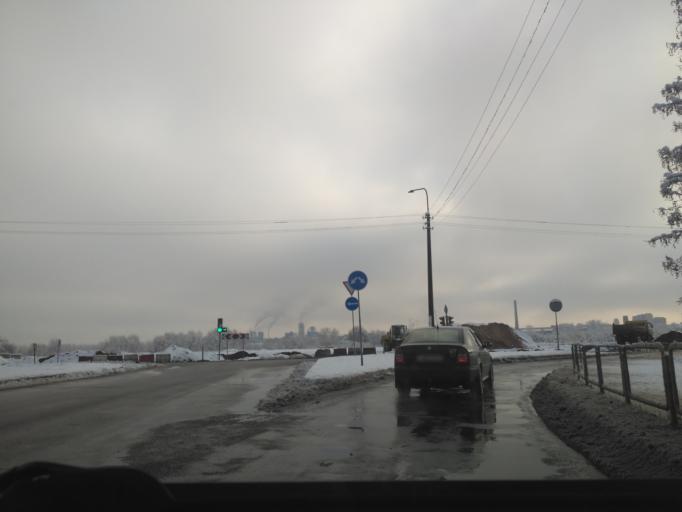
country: BY
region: Minsk
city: Horad Barysaw
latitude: 54.2384
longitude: 28.5131
